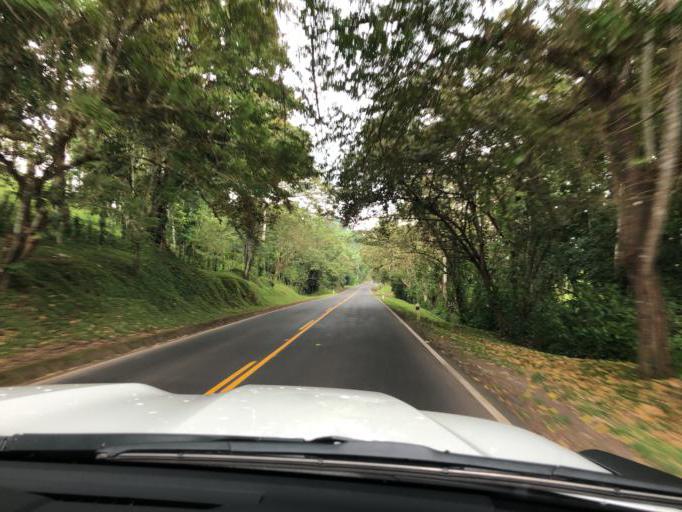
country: NI
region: Chontales
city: Villa Sandino
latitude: 11.9903
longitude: -84.8172
